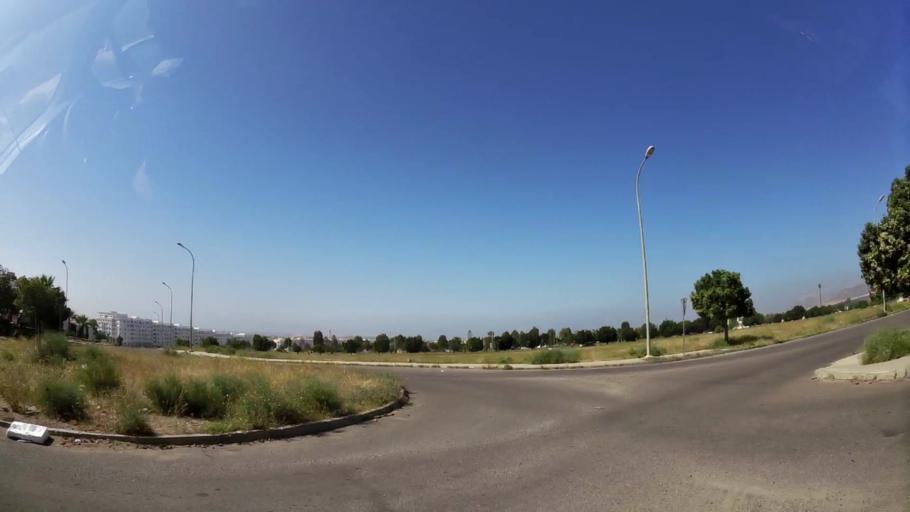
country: MA
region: Souss-Massa-Draa
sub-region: Agadir-Ida-ou-Tnan
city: Agadir
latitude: 30.4382
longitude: -9.5804
